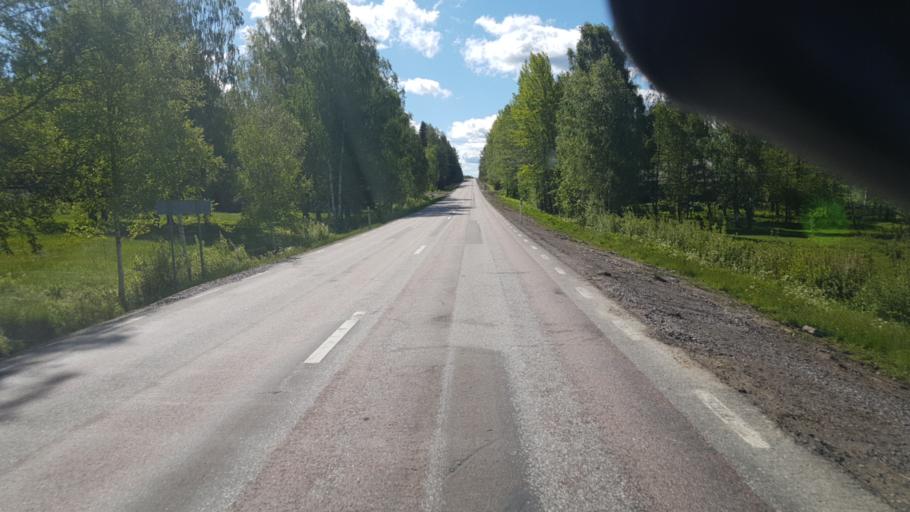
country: SE
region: Vaermland
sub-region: Arvika Kommun
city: Arvika
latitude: 59.5732
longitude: 12.7128
